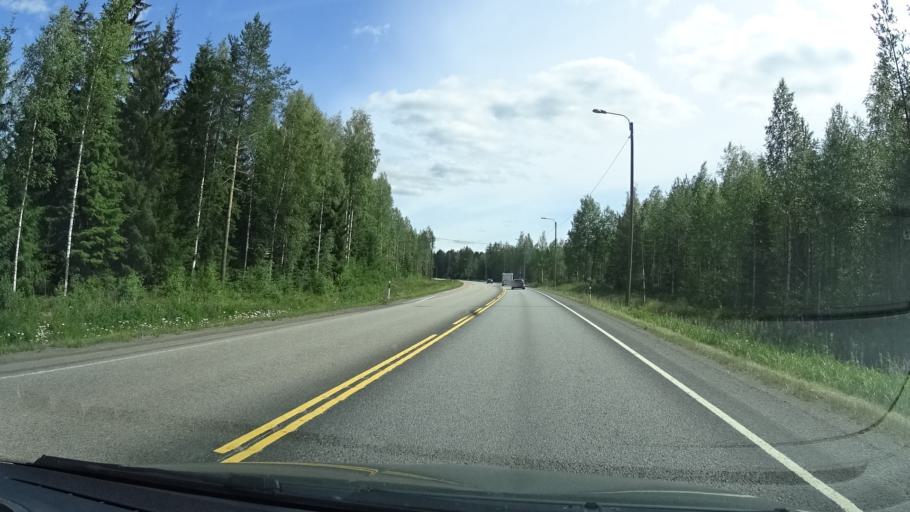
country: FI
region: Central Finland
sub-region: Jyvaeskylae
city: Muurame
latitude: 62.2673
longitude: 25.5199
